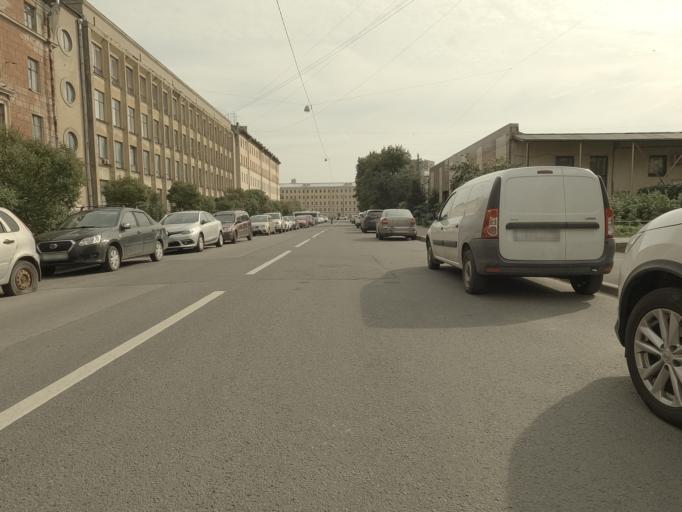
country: RU
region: St.-Petersburg
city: Admiralteisky
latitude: 59.9107
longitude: 30.2925
